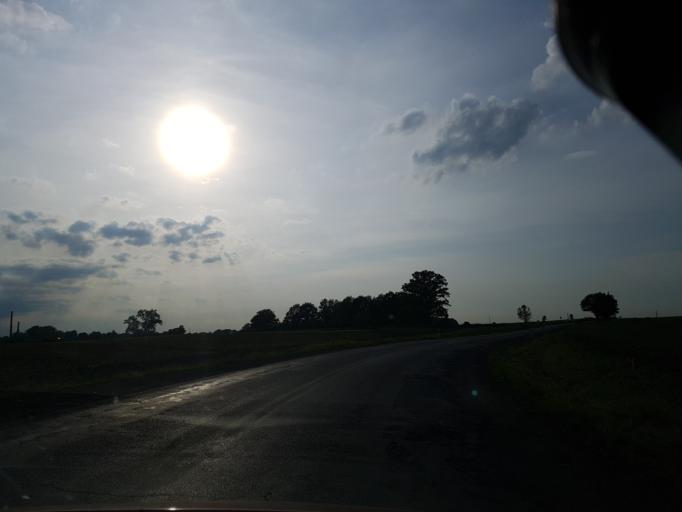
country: PL
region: Lower Silesian Voivodeship
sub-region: Powiat wroclawski
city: Kobierzyce
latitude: 50.9599
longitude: 16.8819
